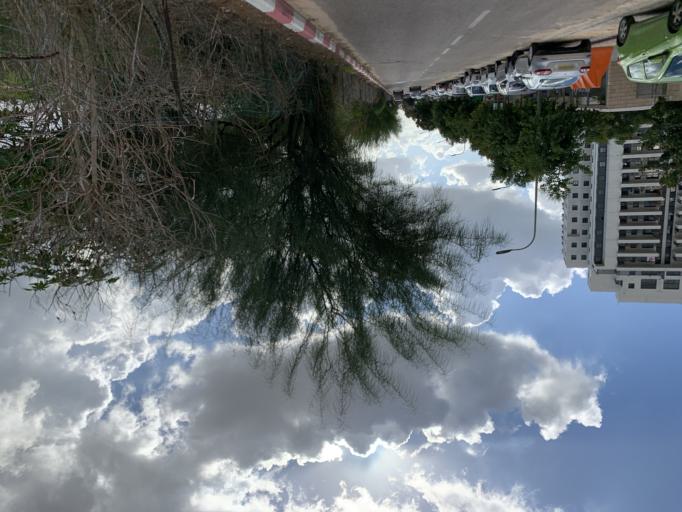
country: IL
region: Central District
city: Hod HaSharon
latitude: 32.1663
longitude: 34.8974
